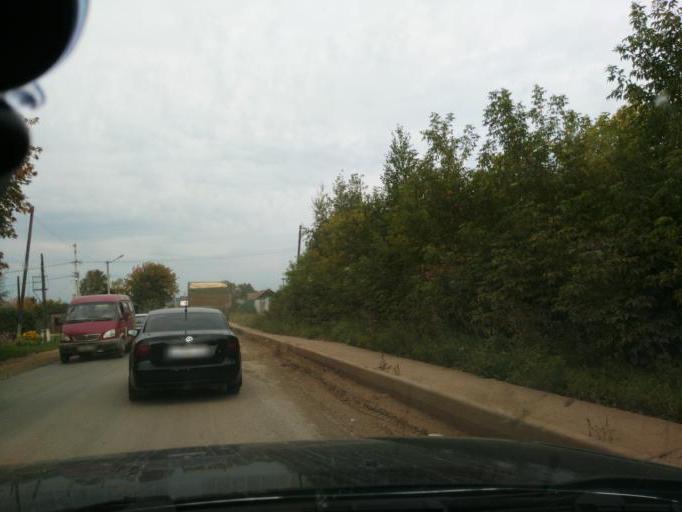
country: RU
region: Perm
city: Kuyeda
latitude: 56.4255
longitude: 55.5816
